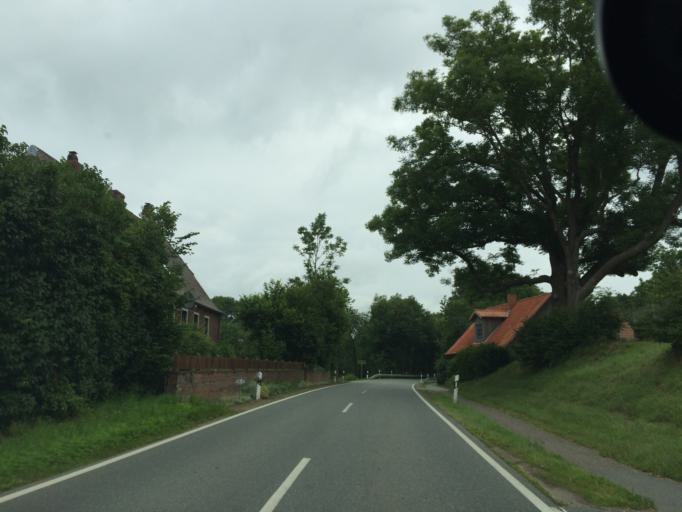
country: DE
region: Schleswig-Holstein
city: Bunsdorf
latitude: 54.3452
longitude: 9.7472
